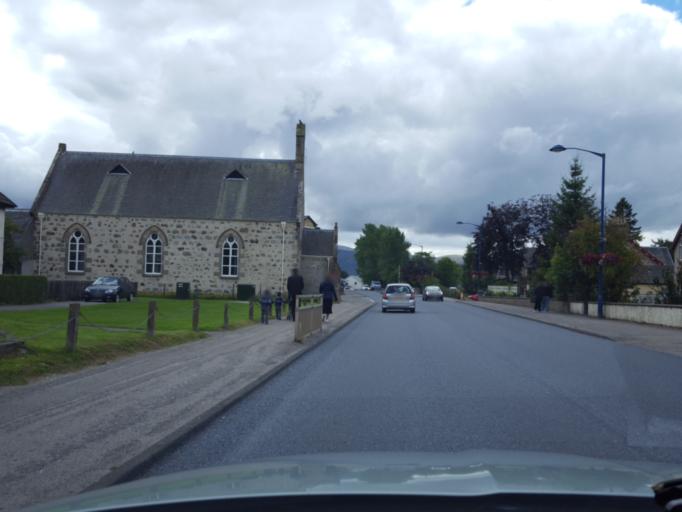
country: GB
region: Scotland
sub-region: Highland
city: Aviemore
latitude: 57.1949
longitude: -3.8291
